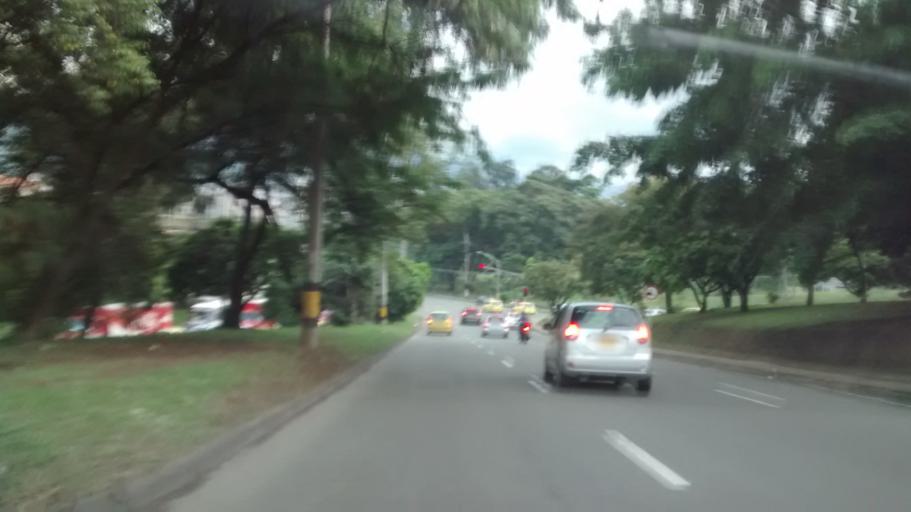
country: CO
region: Antioquia
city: Medellin
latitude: 6.2674
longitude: -75.5766
